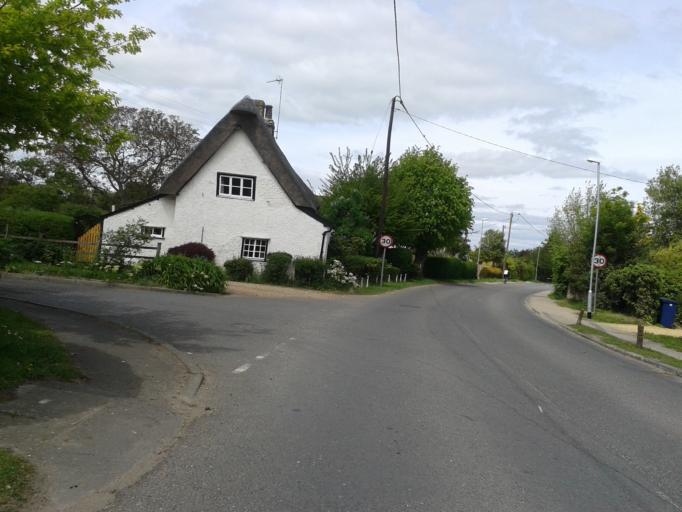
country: GB
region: England
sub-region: Cambridgeshire
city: Haslingfield
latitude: 52.1499
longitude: 0.0491
